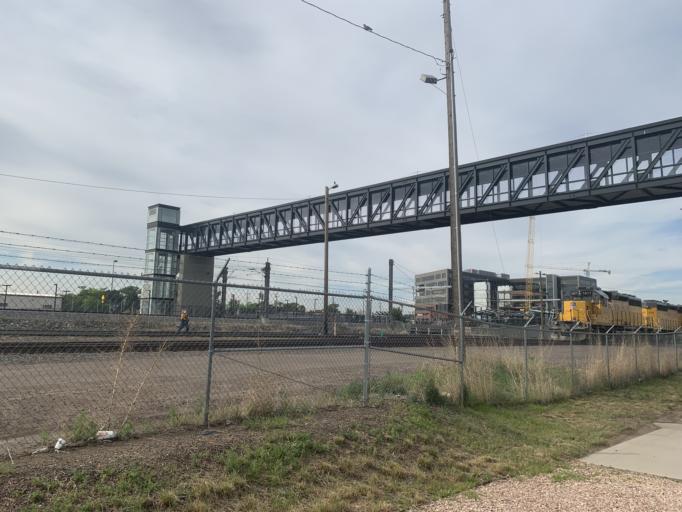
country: US
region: Colorado
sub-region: Denver County
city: Denver
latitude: 39.7721
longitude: -104.9730
